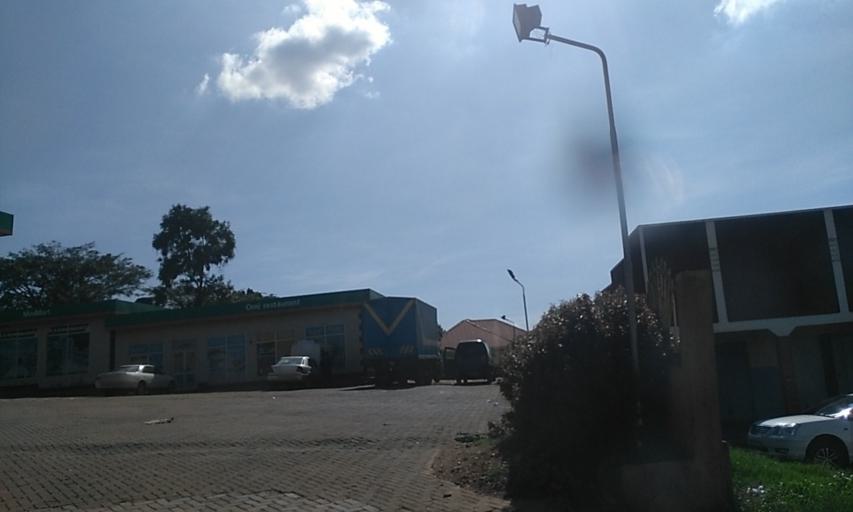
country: UG
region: Central Region
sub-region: Wakiso District
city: Wakiso
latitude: 0.4058
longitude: 32.5421
